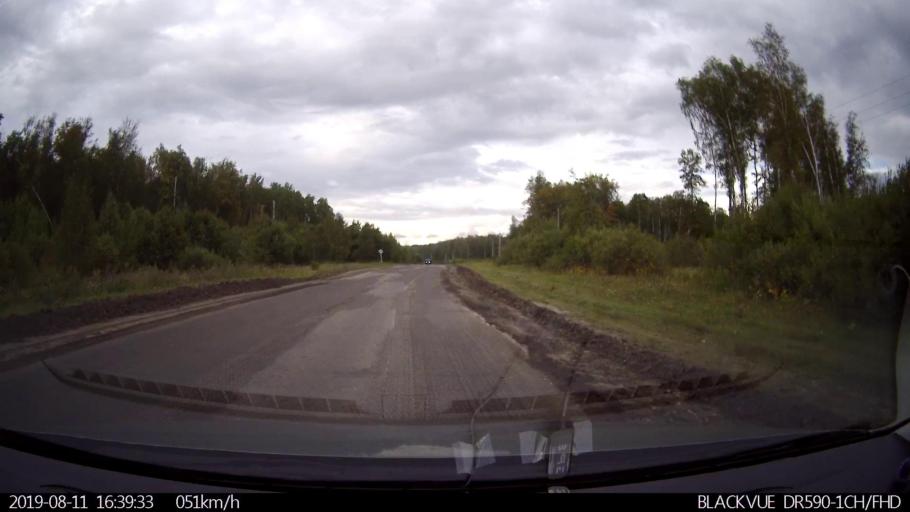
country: RU
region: Ulyanovsk
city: Mayna
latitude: 54.1406
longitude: 47.6381
